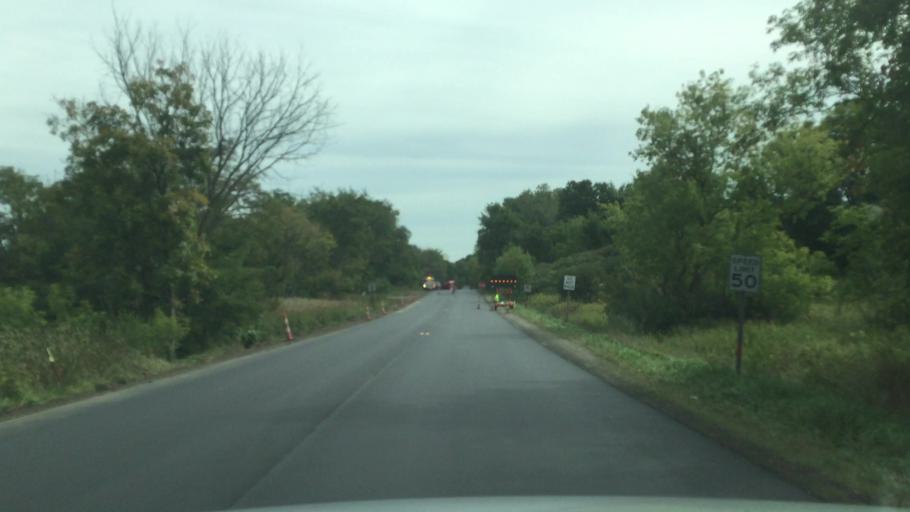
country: US
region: Michigan
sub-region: Oakland County
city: Holly
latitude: 42.8137
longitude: -83.6013
